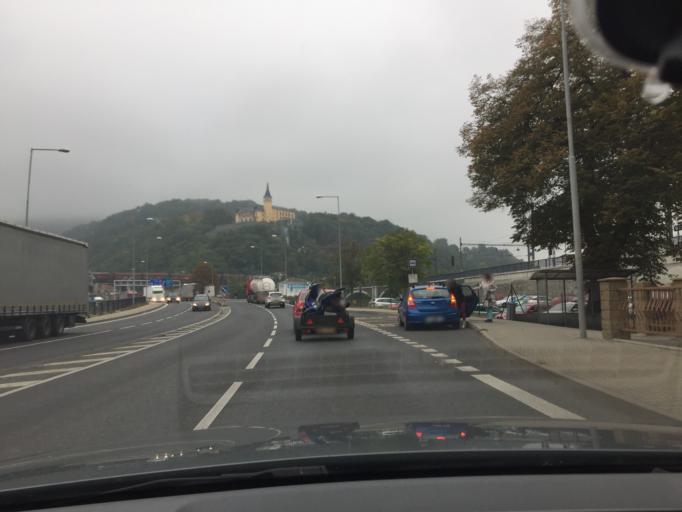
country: CZ
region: Ustecky
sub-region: Okres Usti nad Labem
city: Usti nad Labem
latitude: 50.6588
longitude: 14.0443
